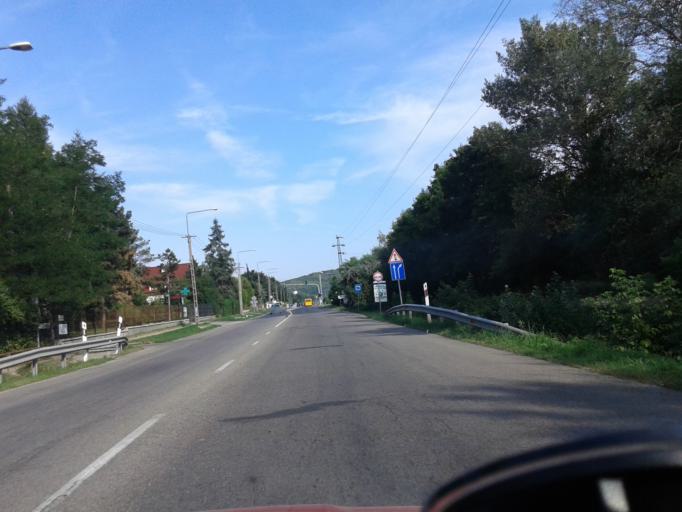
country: HU
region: Pest
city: Godollo
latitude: 47.6006
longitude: 19.3824
